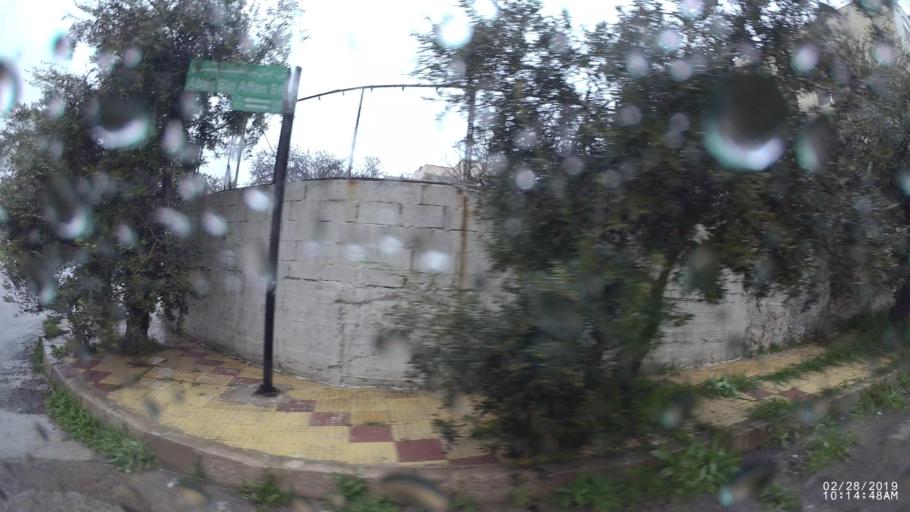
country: JO
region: Amman
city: Al Jubayhah
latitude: 32.0114
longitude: 35.8880
